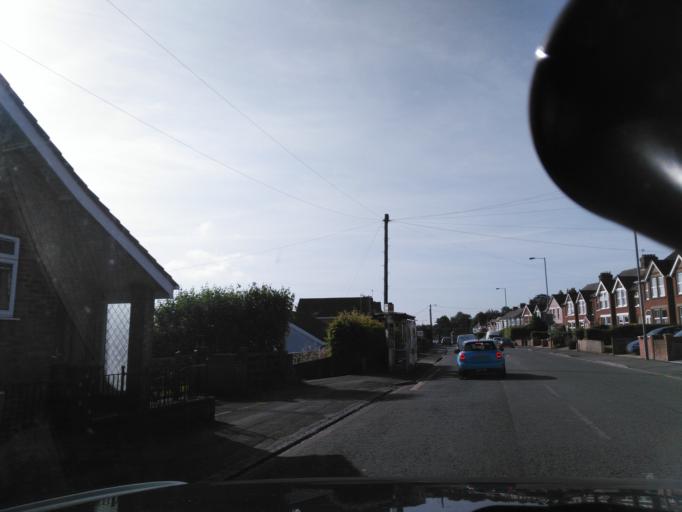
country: GB
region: England
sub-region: Wiltshire
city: Salisbury
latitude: 51.0823
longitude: -1.8191
